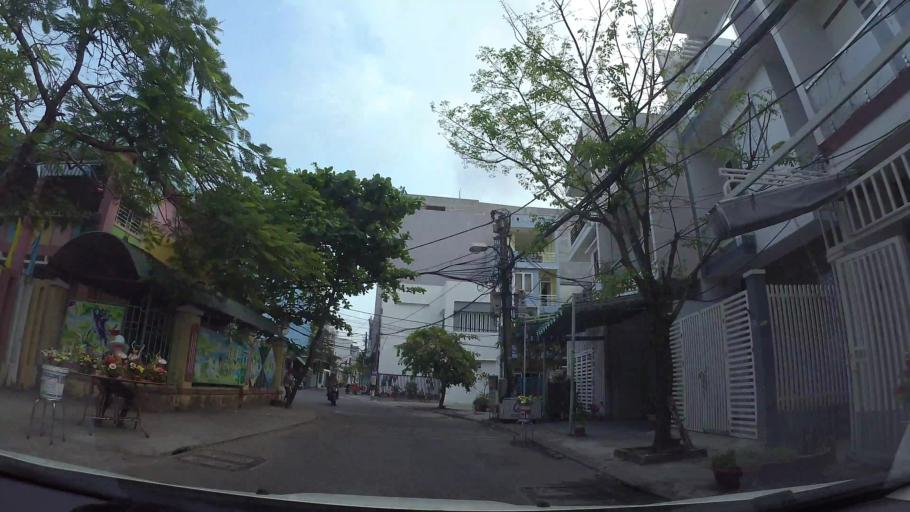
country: VN
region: Da Nang
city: Son Tra
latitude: 16.0623
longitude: 108.2420
